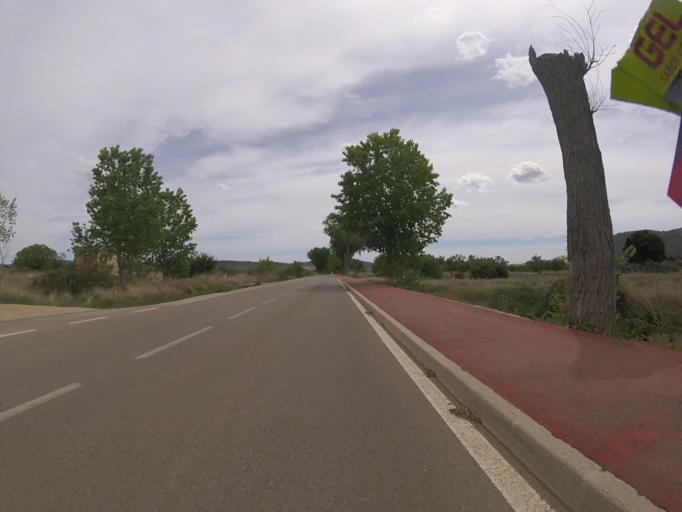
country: ES
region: Valencia
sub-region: Provincia de Castello
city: Cabanes
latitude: 40.1643
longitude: 0.0183
